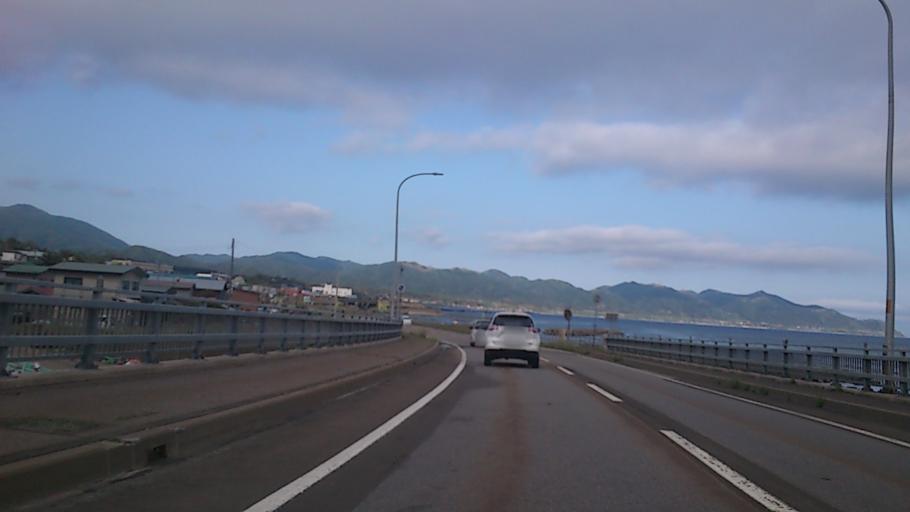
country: JP
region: Aomori
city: Shimokizukuri
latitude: 41.4246
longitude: 140.0949
